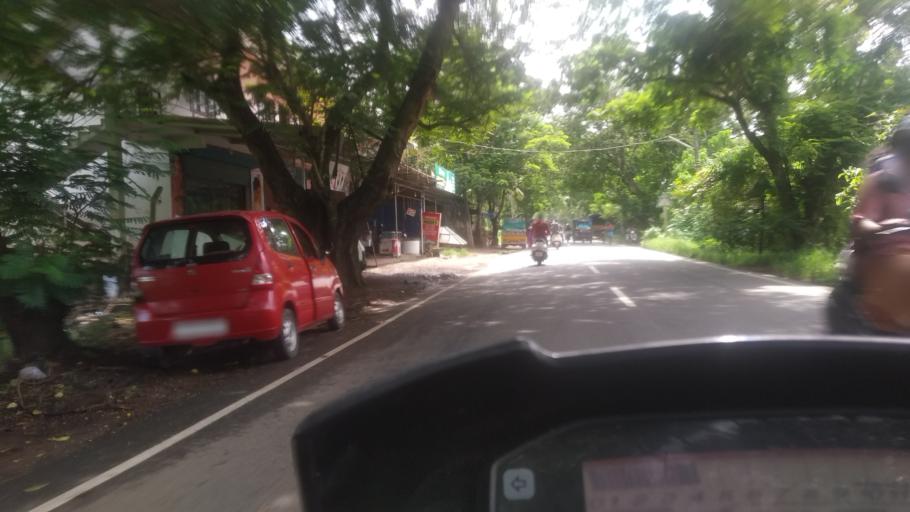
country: IN
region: Kerala
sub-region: Ernakulam
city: Elur
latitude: 10.1306
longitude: 76.2897
